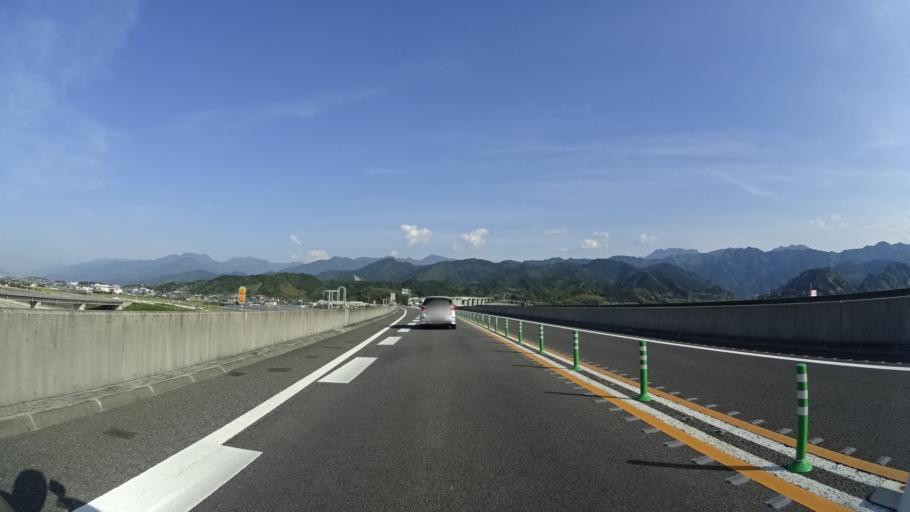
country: JP
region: Ehime
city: Saijo
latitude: 33.8963
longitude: 133.0795
